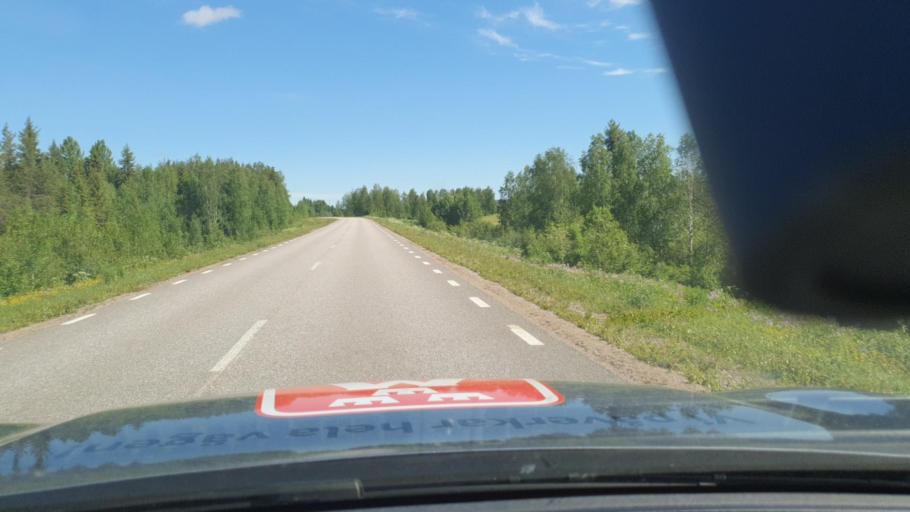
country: SE
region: Norrbotten
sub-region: Overkalix Kommun
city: OEverkalix
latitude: 66.7602
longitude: 22.6792
